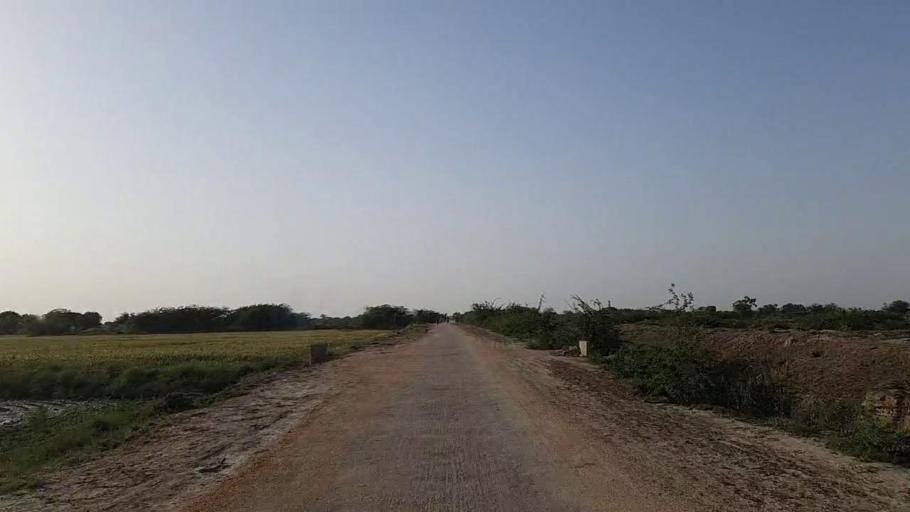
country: PK
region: Sindh
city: Jati
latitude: 24.3307
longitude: 68.1587
